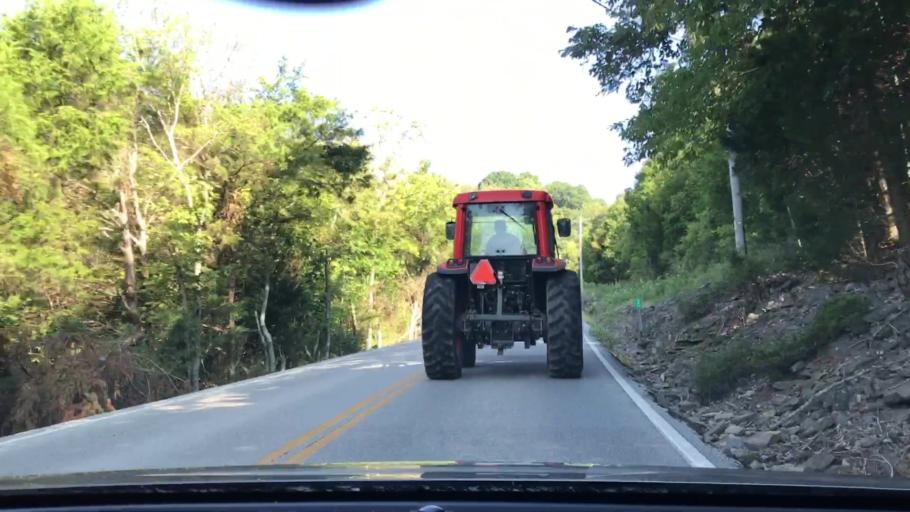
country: US
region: Tennessee
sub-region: Smith County
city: Carthage
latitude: 36.2944
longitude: -85.9537
